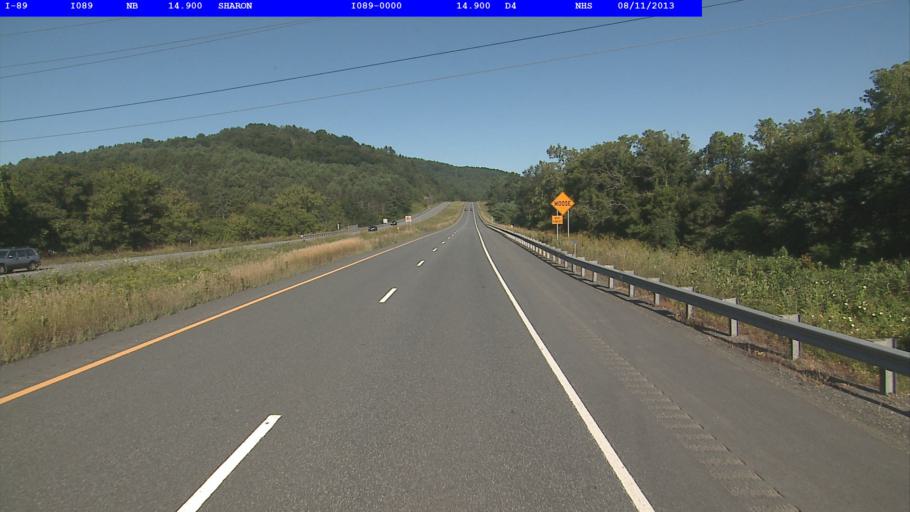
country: US
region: Vermont
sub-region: Windsor County
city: Woodstock
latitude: 43.7824
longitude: -72.4809
